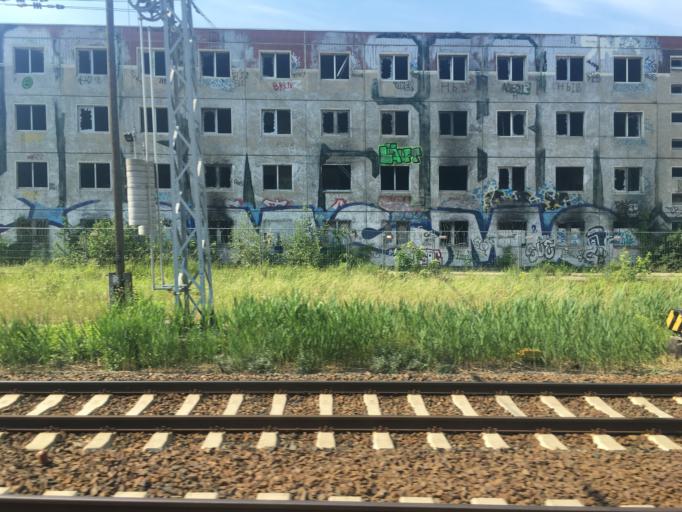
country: DE
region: Berlin
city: Prenzlauer Berg Bezirk
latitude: 52.5420
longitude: 13.4344
